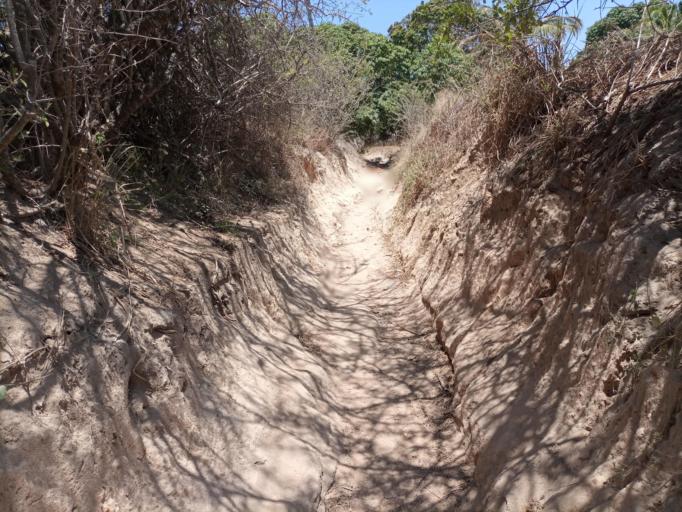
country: MZ
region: Nampula
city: Nacala
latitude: -14.5238
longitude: 40.6794
